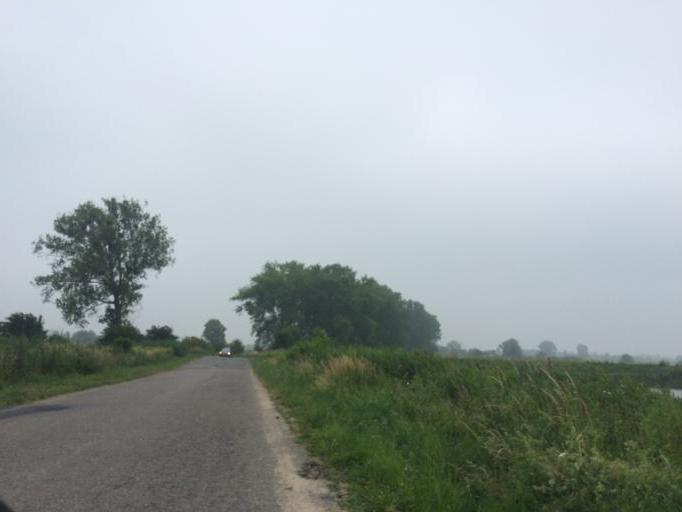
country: PL
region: Lublin Voivodeship
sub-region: Powiat pulawski
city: Markuszow
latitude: 51.3695
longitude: 22.2577
